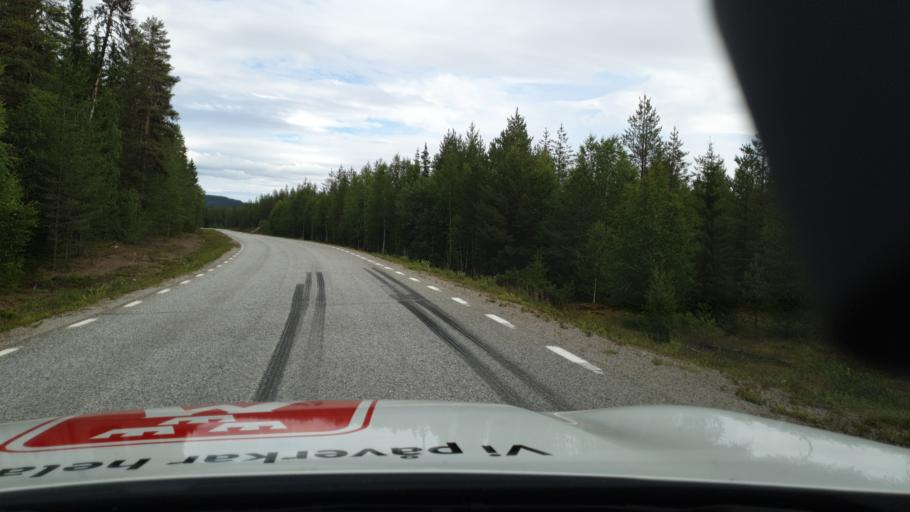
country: SE
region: Vaesterbotten
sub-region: Sorsele Kommun
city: Sorsele
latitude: 65.5176
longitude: 17.3814
